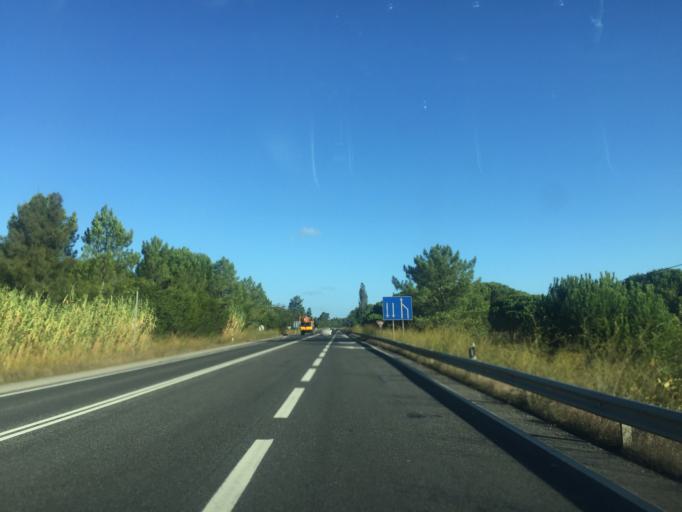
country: PT
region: Lisbon
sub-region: Azambuja
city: Alcoentre
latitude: 39.2521
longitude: -8.9522
